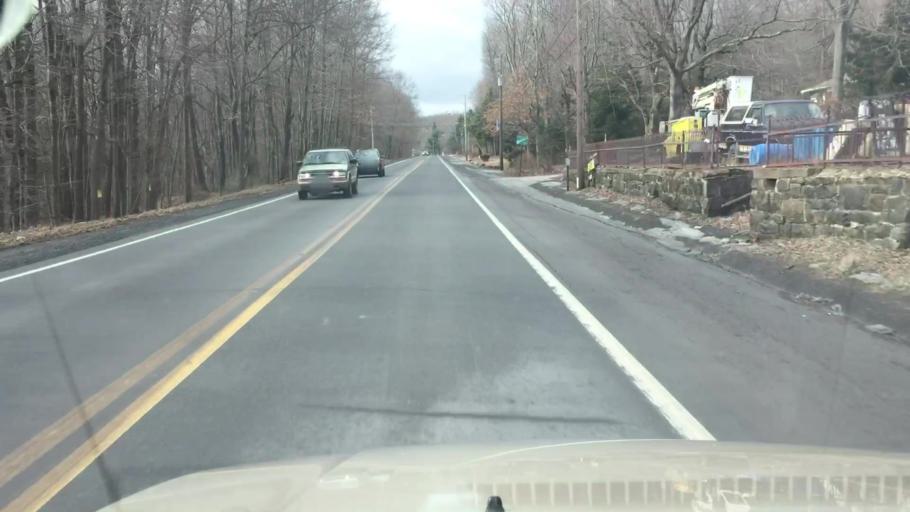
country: US
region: Pennsylvania
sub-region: Luzerne County
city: Harleigh
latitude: 40.9861
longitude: -75.9467
